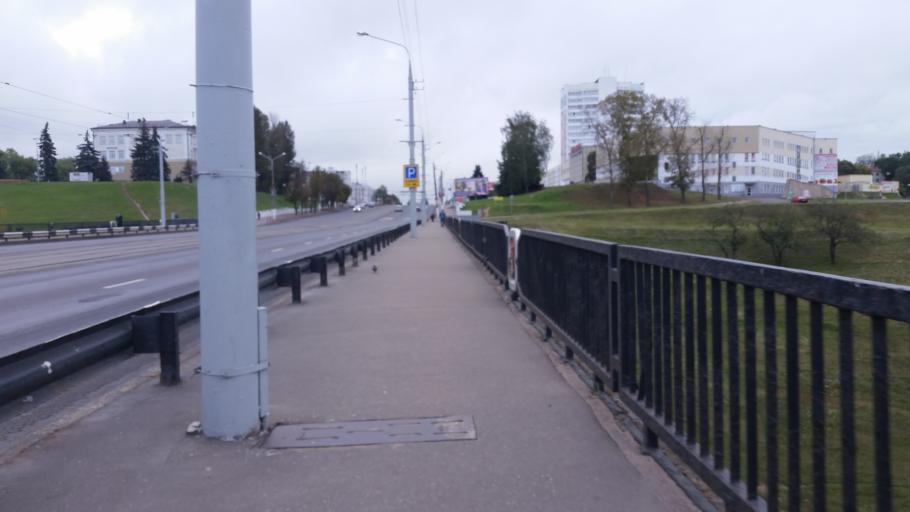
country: BY
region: Vitebsk
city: Vitebsk
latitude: 55.1838
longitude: 30.1974
